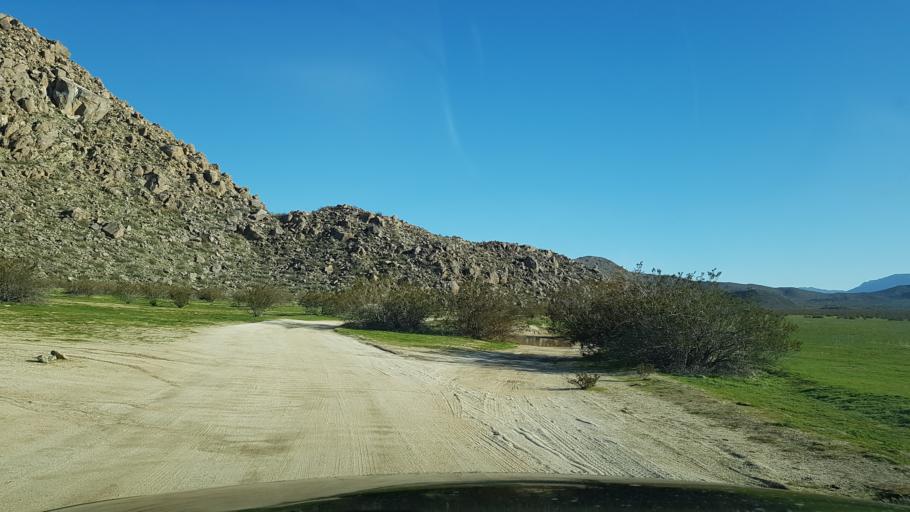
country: US
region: California
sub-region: San Diego County
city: Julian
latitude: 33.0332
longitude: -116.4004
